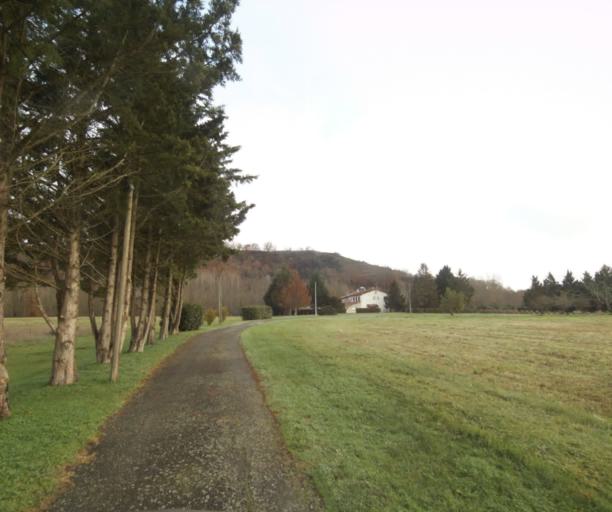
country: FR
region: Midi-Pyrenees
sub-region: Departement de la Haute-Garonne
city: Villemur-sur-Tarn
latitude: 43.8875
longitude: 1.4814
